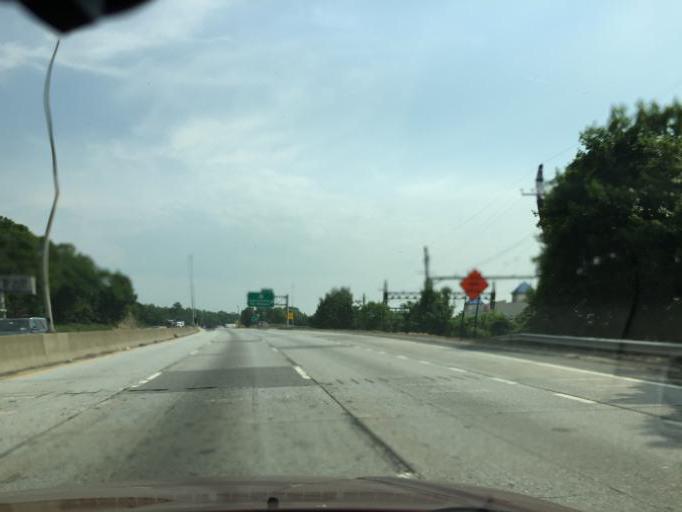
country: US
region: New York
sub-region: Westchester County
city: Pelham Manor
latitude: 40.8966
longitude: -73.7974
